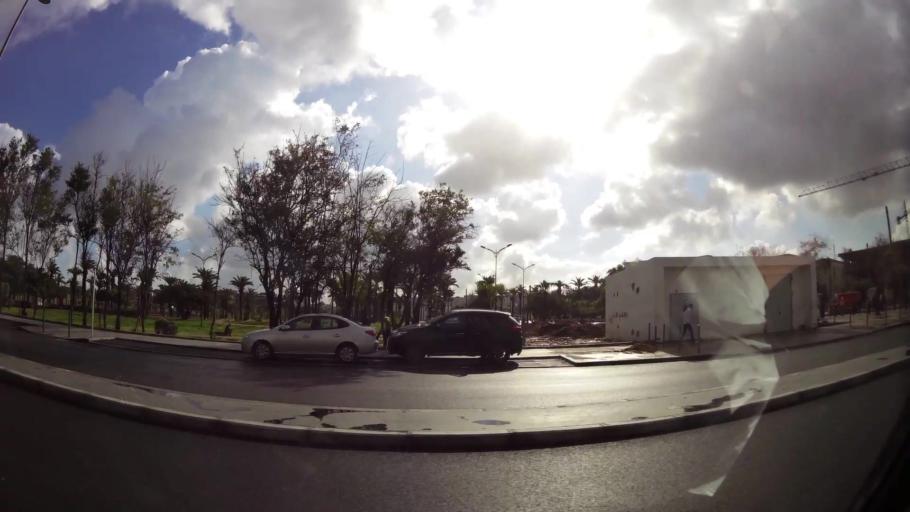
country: MA
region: Grand Casablanca
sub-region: Mediouna
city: Tit Mellil
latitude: 33.6011
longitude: -7.5308
